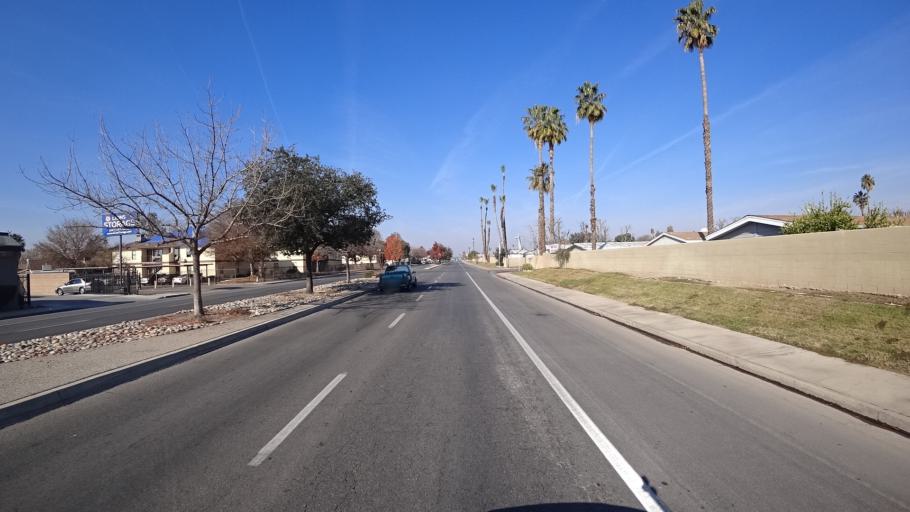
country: US
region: California
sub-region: Kern County
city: Bakersfield
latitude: 35.3261
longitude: -119.0100
